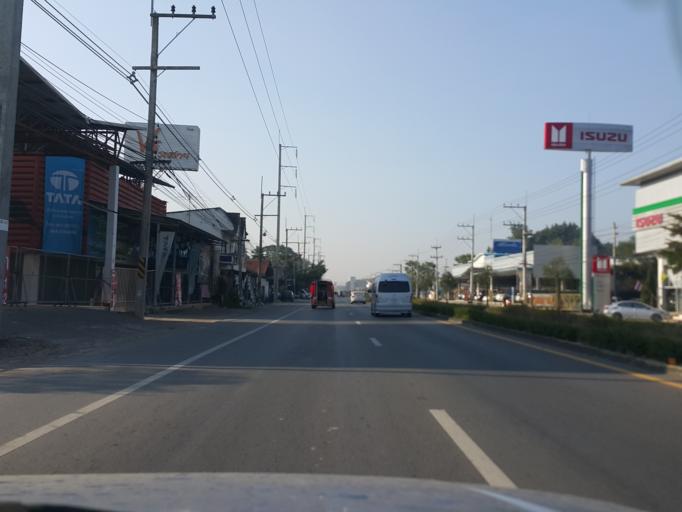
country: TH
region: Chiang Mai
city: San Pa Tong
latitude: 18.6436
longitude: 98.9016
